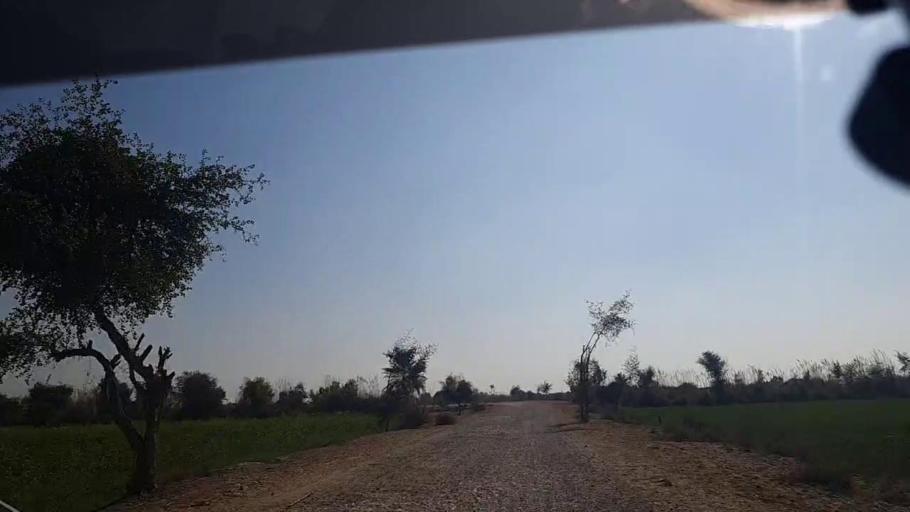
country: PK
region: Sindh
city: Khanpur
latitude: 27.5661
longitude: 69.3044
